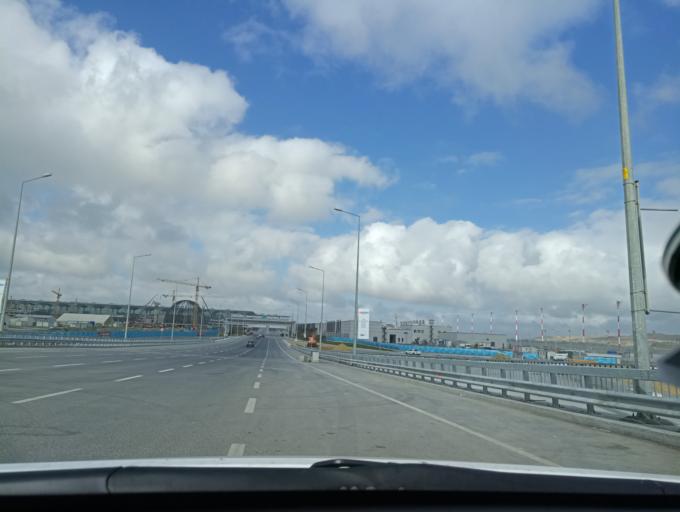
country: TR
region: Istanbul
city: Durusu
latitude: 41.2483
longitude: 28.7467
